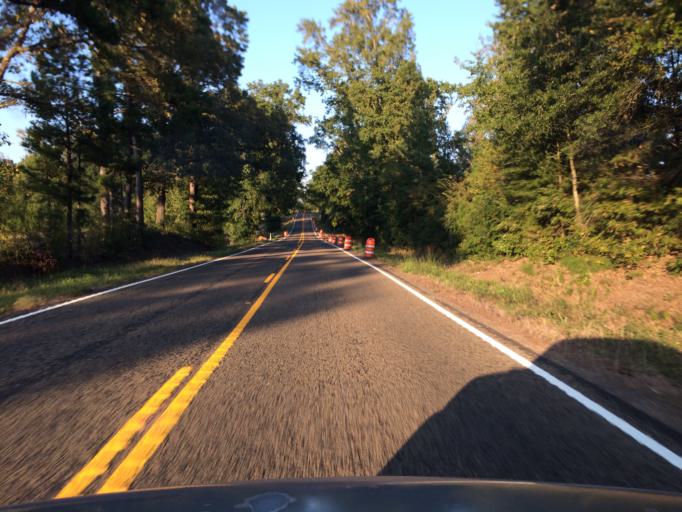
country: US
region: Texas
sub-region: Wood County
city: Quitman
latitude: 32.7378
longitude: -95.2977
